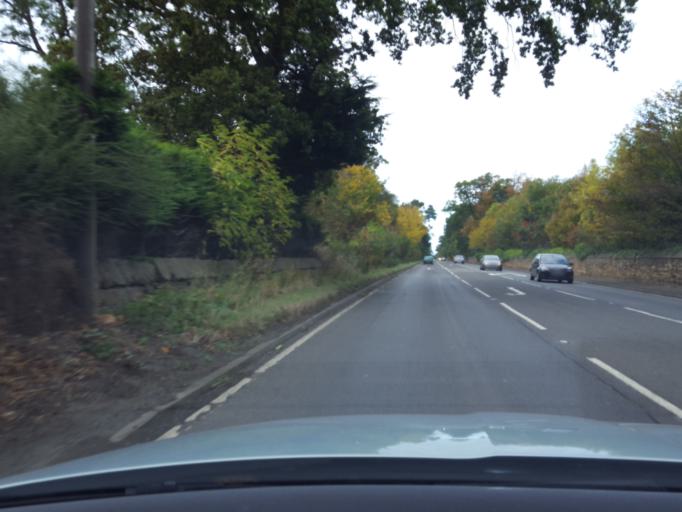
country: GB
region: Scotland
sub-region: Fife
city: Pathhead
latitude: 55.8778
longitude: -2.9860
